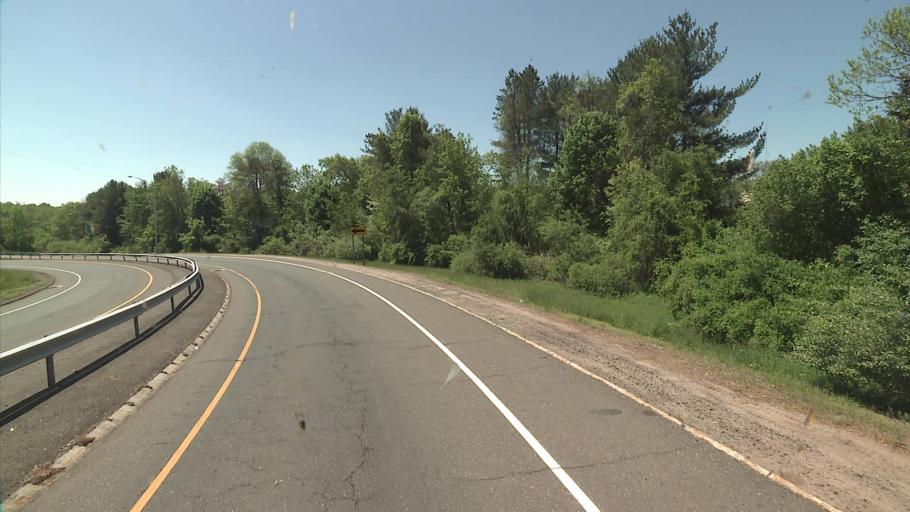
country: US
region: Connecticut
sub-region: Hartford County
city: Farmington
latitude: 41.7059
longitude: -72.8053
